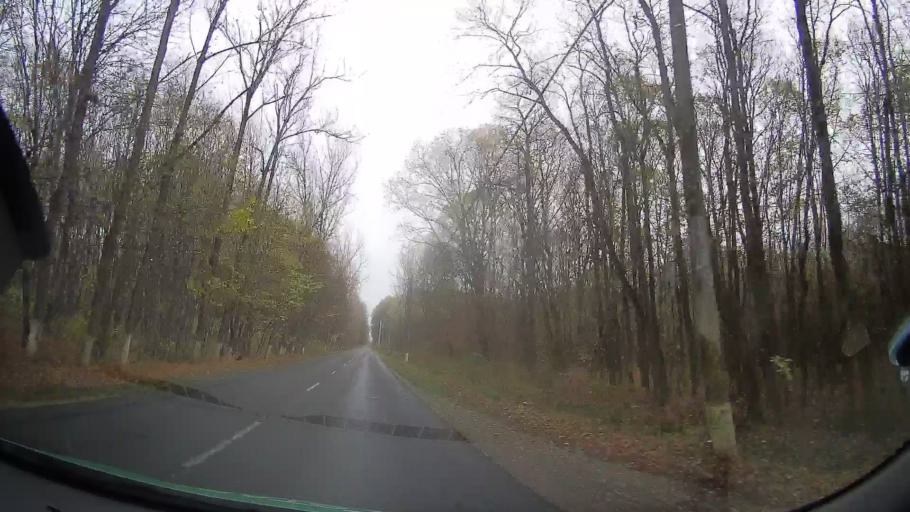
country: RO
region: Ilfov
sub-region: Comuna Snagov
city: Snagov
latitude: 44.7162
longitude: 26.1979
